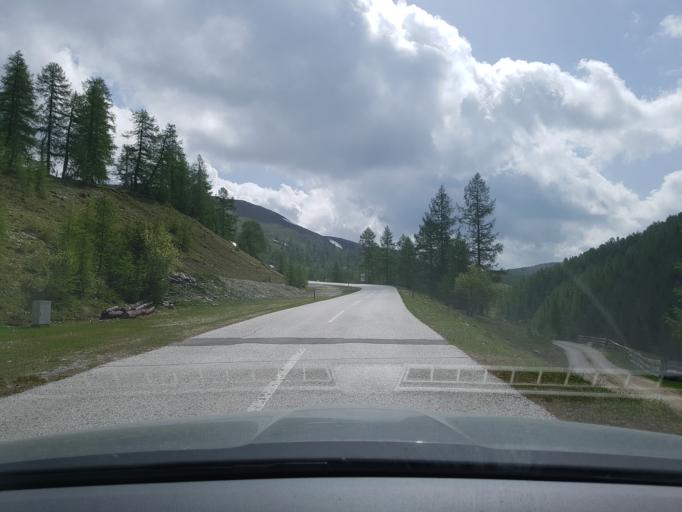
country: AT
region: Salzburg
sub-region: Politischer Bezirk Tamsweg
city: Thomatal
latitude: 46.9400
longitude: 13.7396
